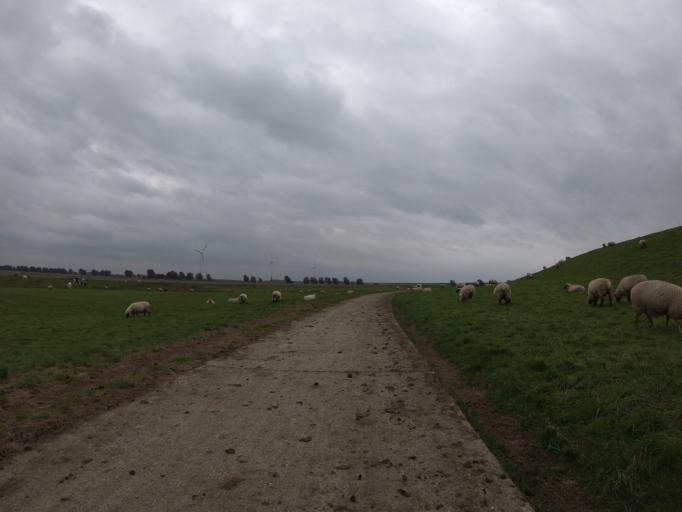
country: DE
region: Lower Saxony
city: Wirdum
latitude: 53.4889
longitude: 7.0374
